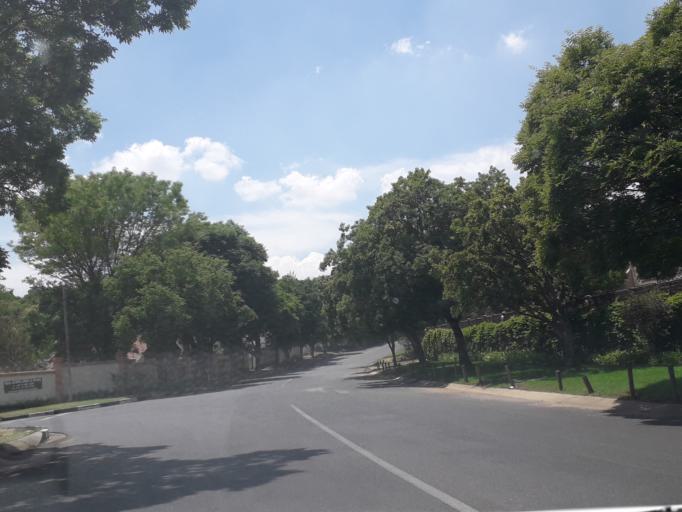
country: ZA
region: Gauteng
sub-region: City of Johannesburg Metropolitan Municipality
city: Midrand
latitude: -26.0362
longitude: 28.0719
